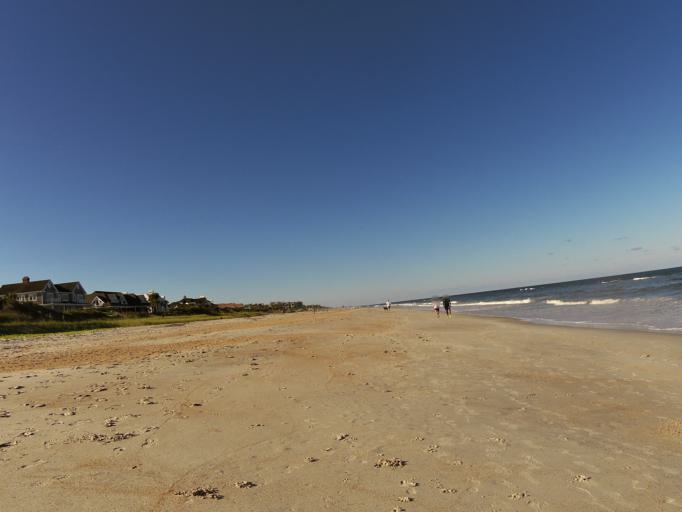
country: US
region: Florida
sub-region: Saint Johns County
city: Sawgrass
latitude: 30.1895
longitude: -81.3628
